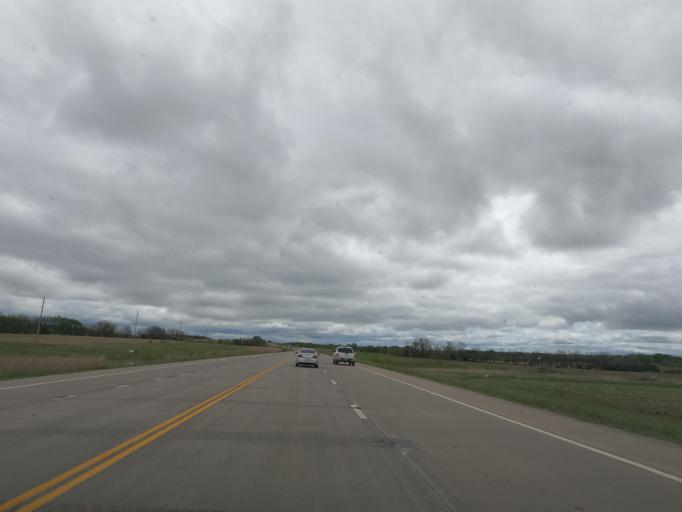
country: US
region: Kansas
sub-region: Elk County
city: Howard
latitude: 37.6348
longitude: -96.1916
